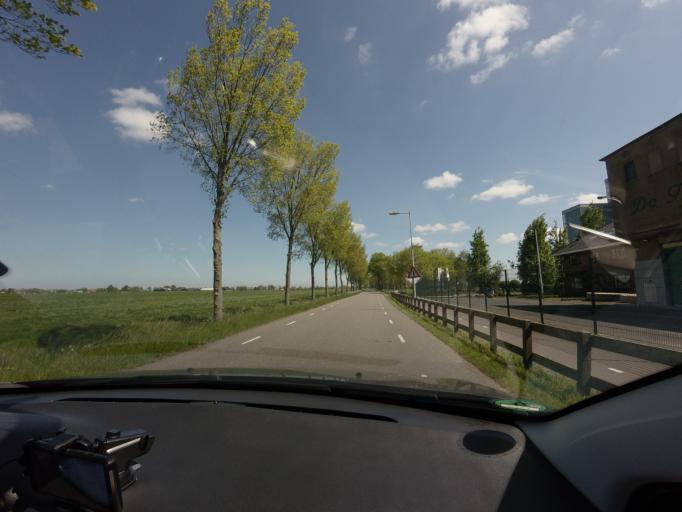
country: NL
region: North Holland
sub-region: Gemeente Beemster
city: Halfweg
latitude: 52.5568
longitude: 4.8749
